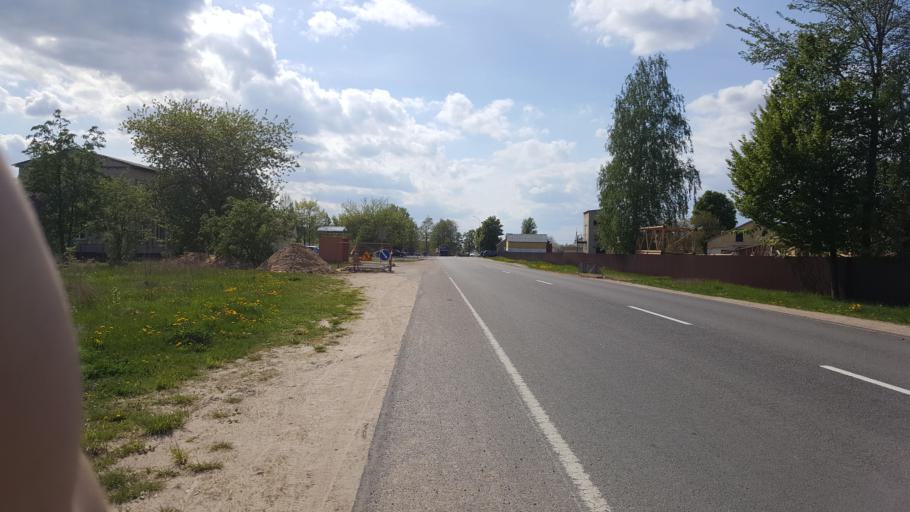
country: BY
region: Brest
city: Kamyanyets
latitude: 52.4024
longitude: 23.8379
